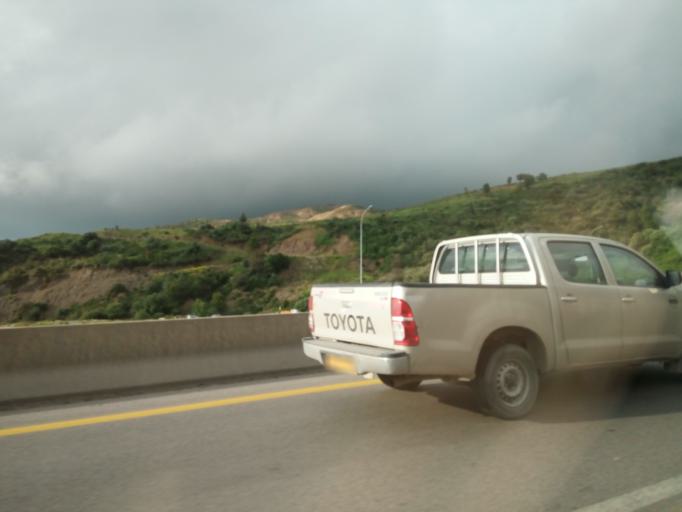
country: DZ
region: Boumerdes
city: Arbatache
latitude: 36.5752
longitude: 3.4088
